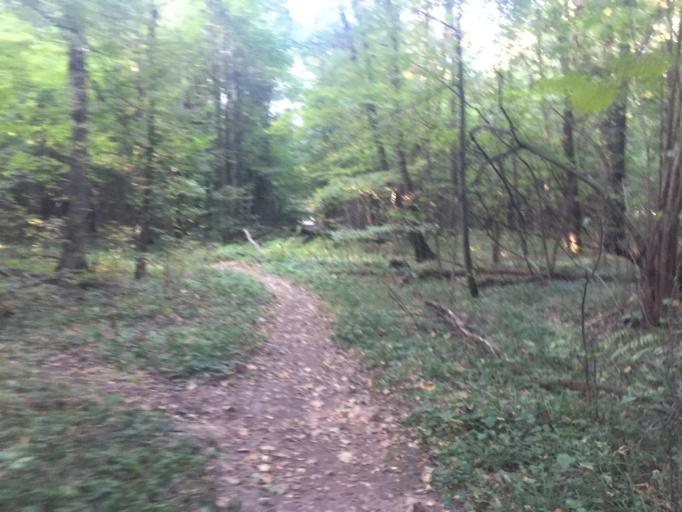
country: RU
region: Moscow
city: Gol'yanovo
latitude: 55.8437
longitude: 37.7966
